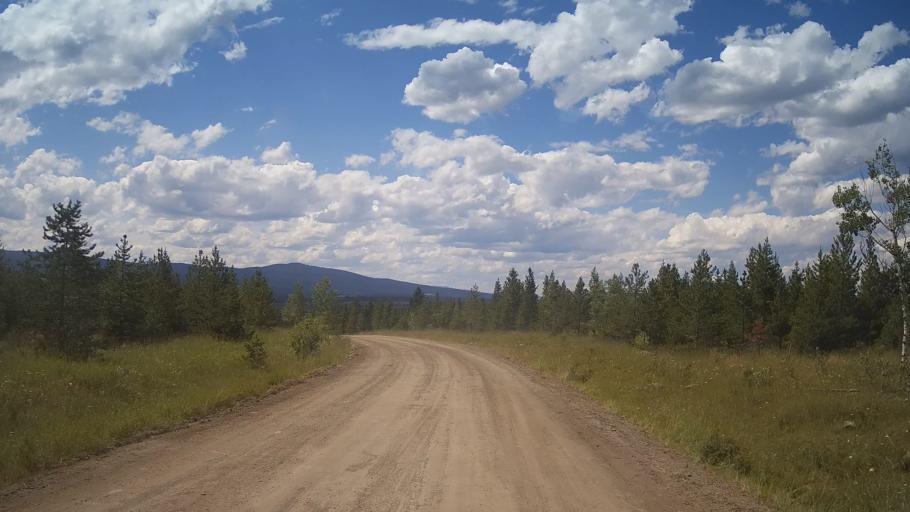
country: CA
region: British Columbia
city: Lillooet
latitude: 51.3416
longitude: -121.9280
